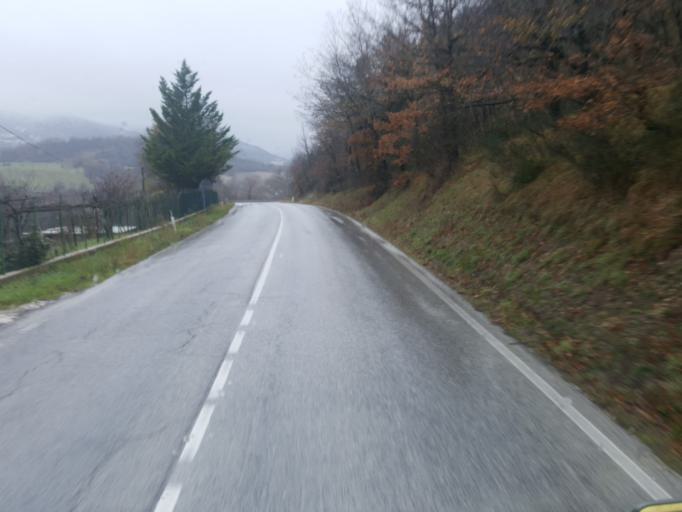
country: IT
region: The Marches
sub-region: Provincia di Ancona
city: Genga
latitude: 43.4274
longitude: 12.9188
